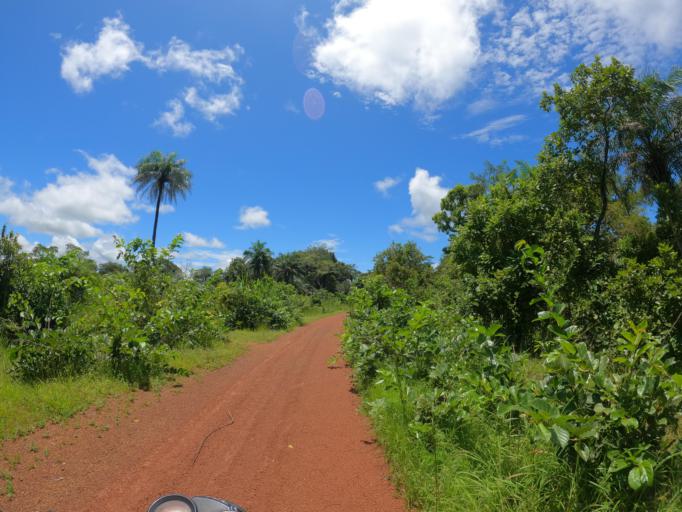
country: SL
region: Northern Province
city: Makeni
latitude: 9.0833
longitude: -12.2687
